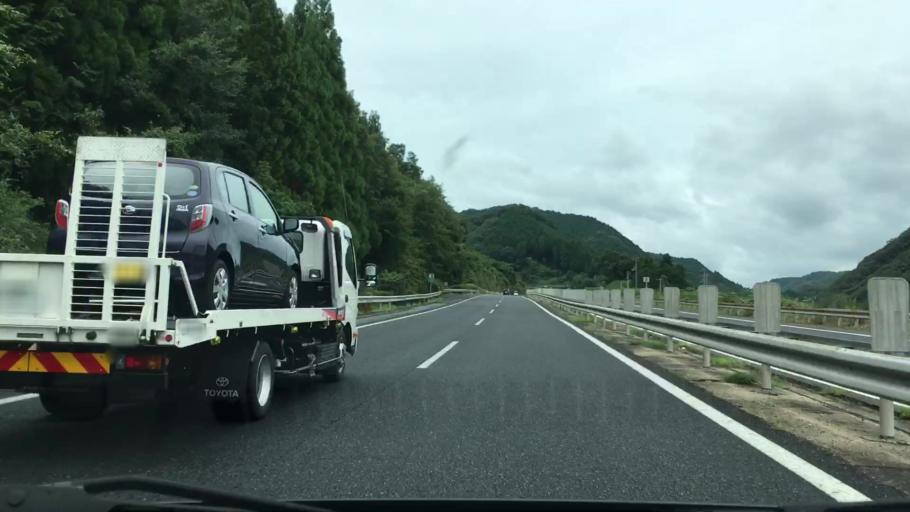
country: JP
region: Hyogo
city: Yamazakicho-nakabirose
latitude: 35.0110
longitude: 134.2999
